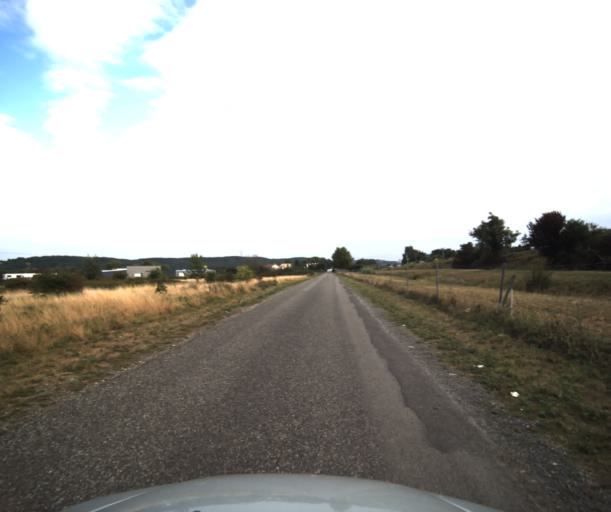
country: FR
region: Midi-Pyrenees
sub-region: Departement de la Haute-Garonne
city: Le Fauga
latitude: 43.4416
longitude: 1.3088
